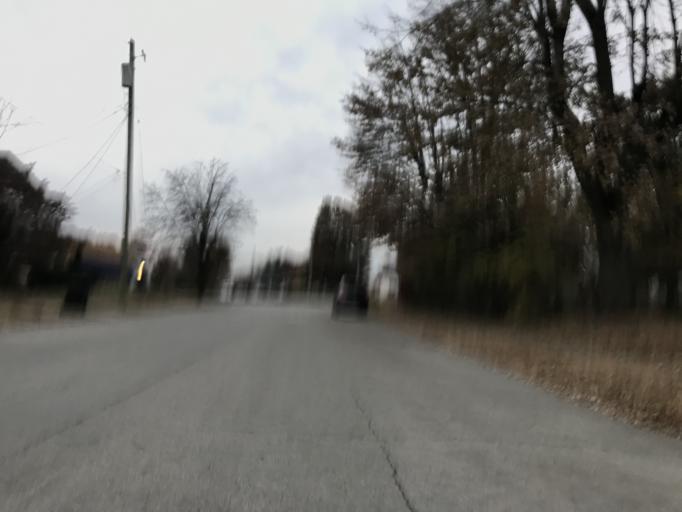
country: US
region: Kentucky
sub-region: Jefferson County
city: Audubon Park
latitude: 38.2185
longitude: -85.7396
